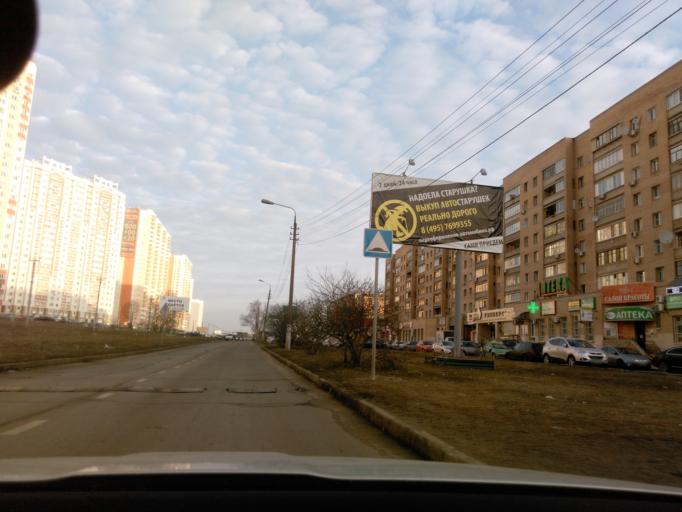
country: RU
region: Moscow
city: Khimki
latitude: 55.9018
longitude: 37.4049
